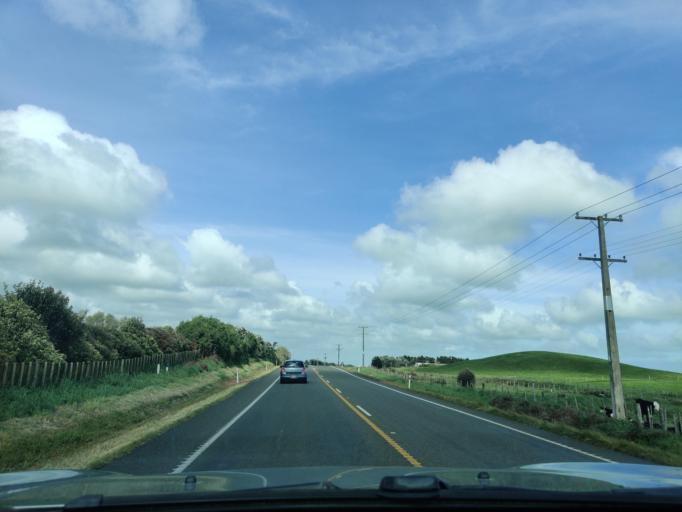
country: NZ
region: Taranaki
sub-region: South Taranaki District
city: Patea
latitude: -39.7721
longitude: 174.6721
